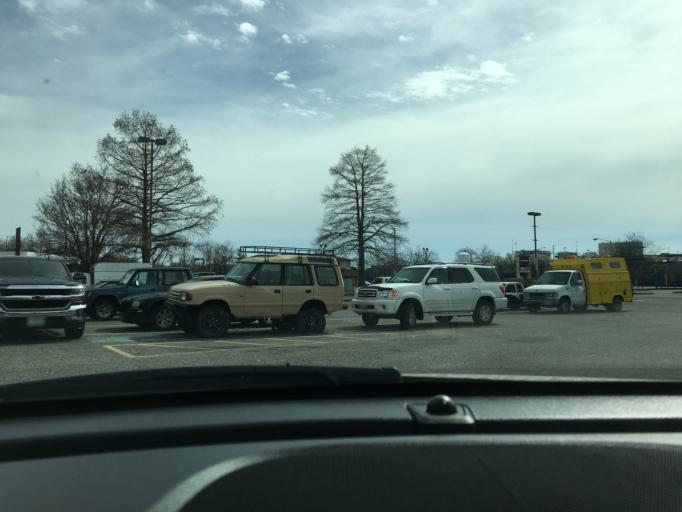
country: US
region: Maryland
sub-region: Wicomico County
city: Salisbury
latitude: 38.3682
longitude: -75.6074
